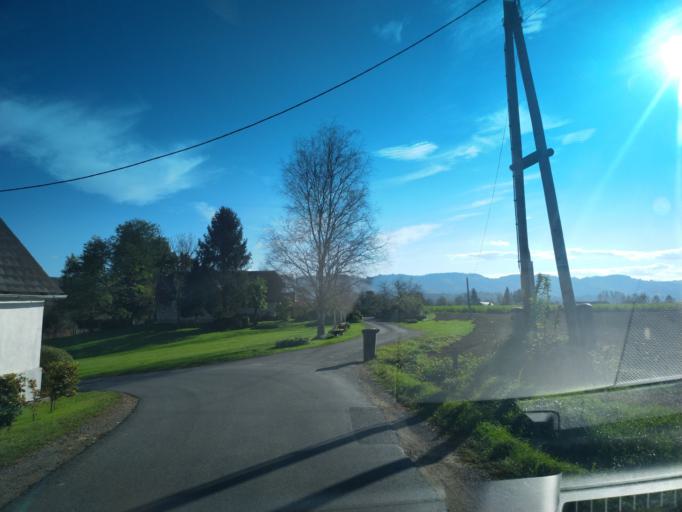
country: AT
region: Styria
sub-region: Politischer Bezirk Leibnitz
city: Sankt Johann im Saggautal
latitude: 46.7065
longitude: 15.3922
